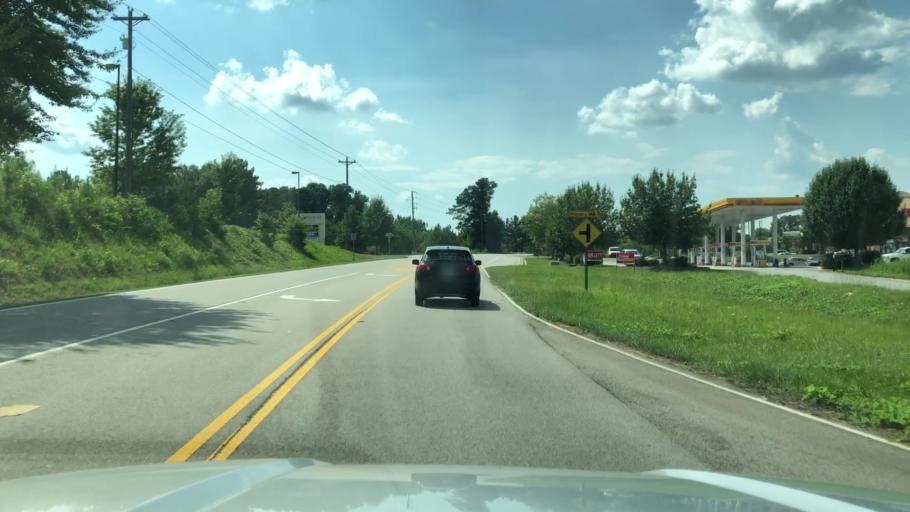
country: US
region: Georgia
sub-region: Paulding County
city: Dallas
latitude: 33.9562
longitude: -84.7858
